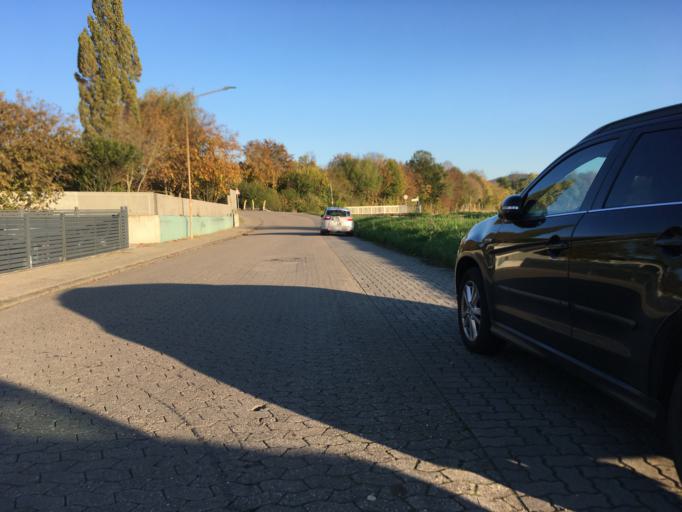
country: DE
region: Hesse
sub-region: Regierungsbezirk Darmstadt
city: Bensheim
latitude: 49.6826
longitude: 8.5958
